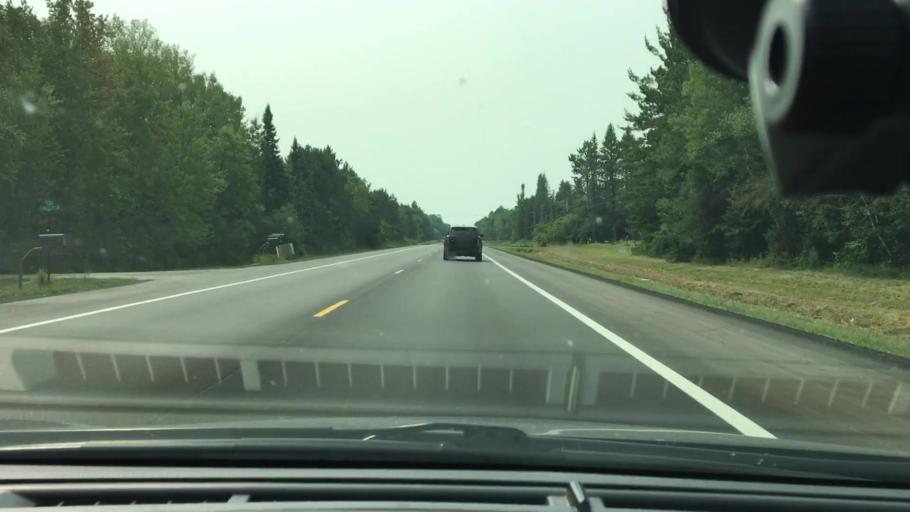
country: US
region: Minnesota
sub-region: Crow Wing County
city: Brainerd
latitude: 46.4482
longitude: -94.1720
